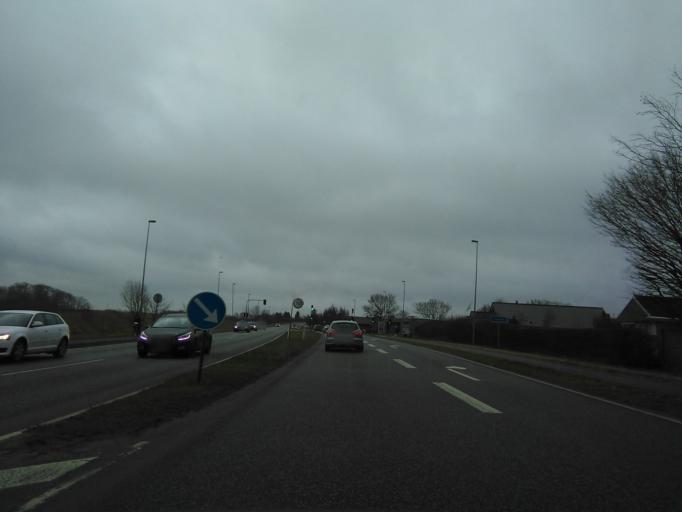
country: DK
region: Central Jutland
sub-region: Arhus Kommune
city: Tranbjerg
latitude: 56.0999
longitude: 10.1398
